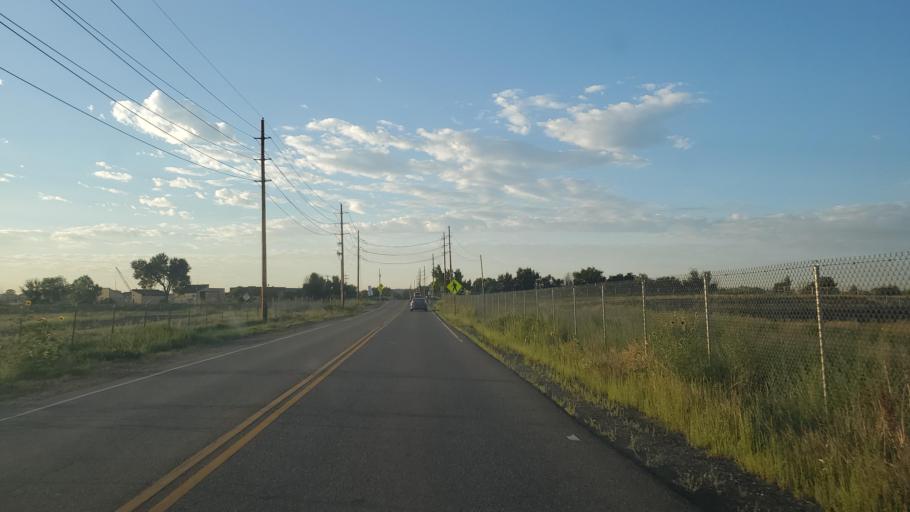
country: US
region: Colorado
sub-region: Adams County
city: Derby
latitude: 39.8759
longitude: -104.9145
